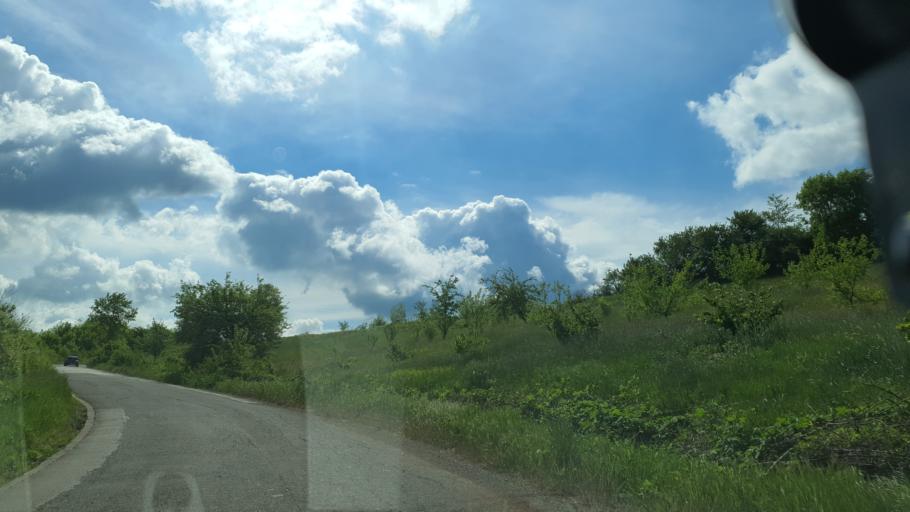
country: RS
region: Central Serbia
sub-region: Pomoravski Okrug
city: Cuprija
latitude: 43.9528
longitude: 21.4841
